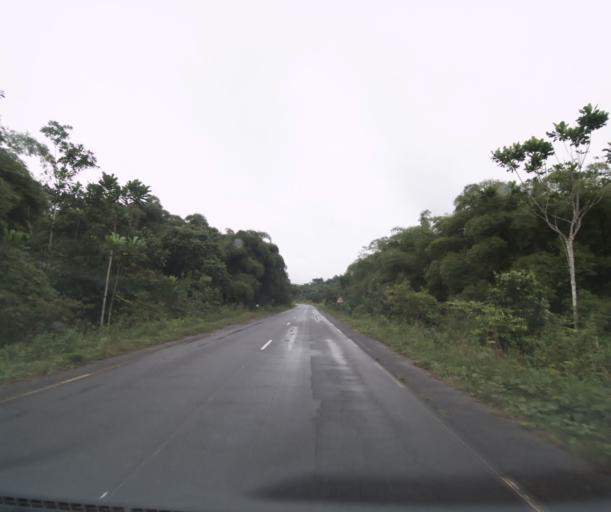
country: CM
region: Littoral
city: Dizangue
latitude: 3.3773
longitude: 10.1030
